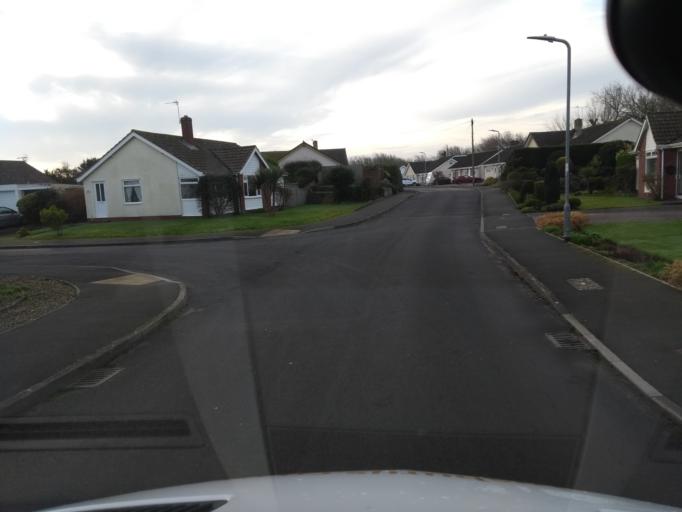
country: GB
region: England
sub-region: Somerset
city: Burnham-on-Sea
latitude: 51.2566
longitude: -3.0049
